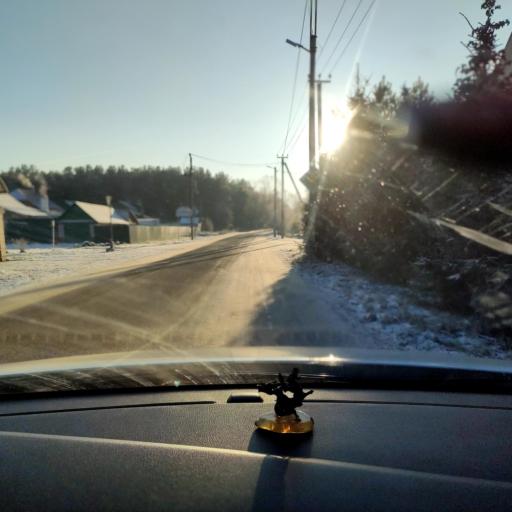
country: RU
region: Tatarstan
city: Stolbishchi
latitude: 55.6758
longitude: 49.1161
